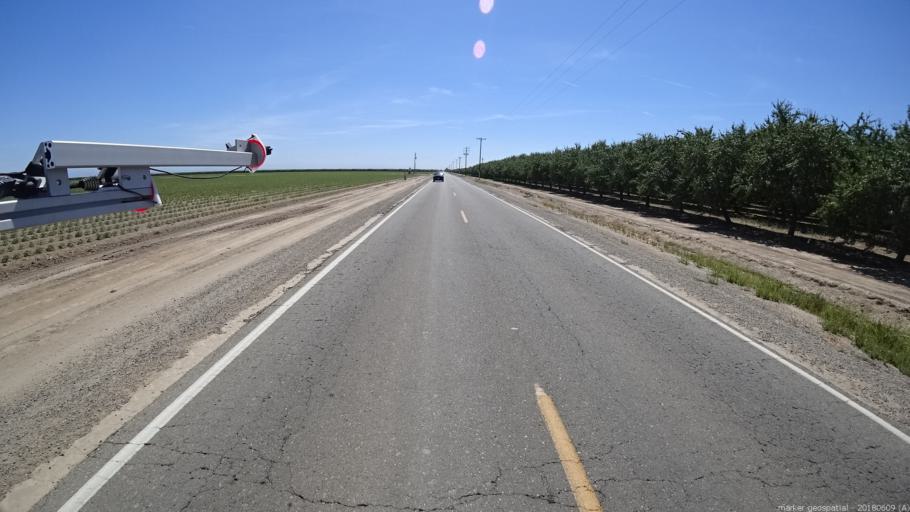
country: US
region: California
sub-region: Madera County
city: Fairmead
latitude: 36.9528
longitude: -120.2269
